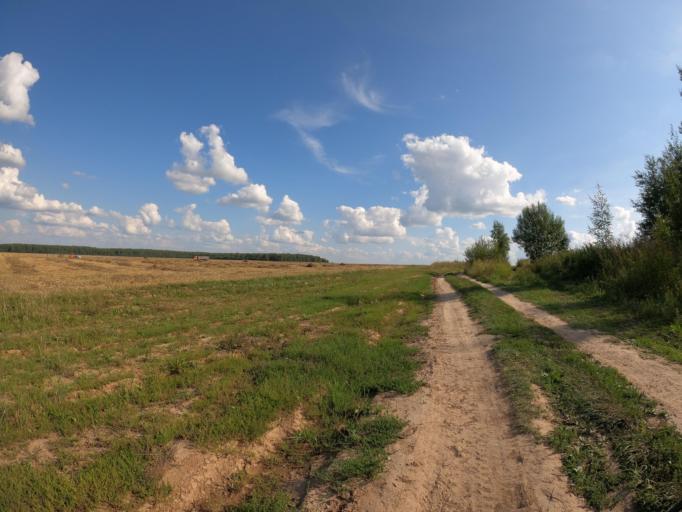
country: RU
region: Moskovskaya
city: Troitskoye
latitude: 55.2249
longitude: 38.4858
